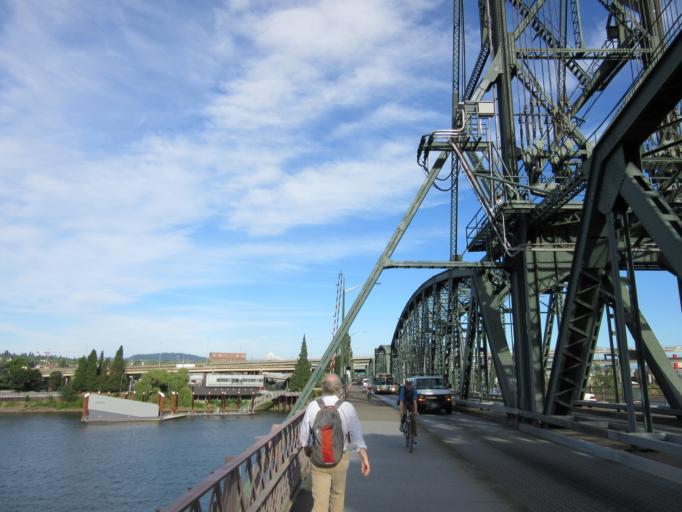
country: US
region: Oregon
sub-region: Multnomah County
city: Portland
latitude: 45.5135
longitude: -122.6718
